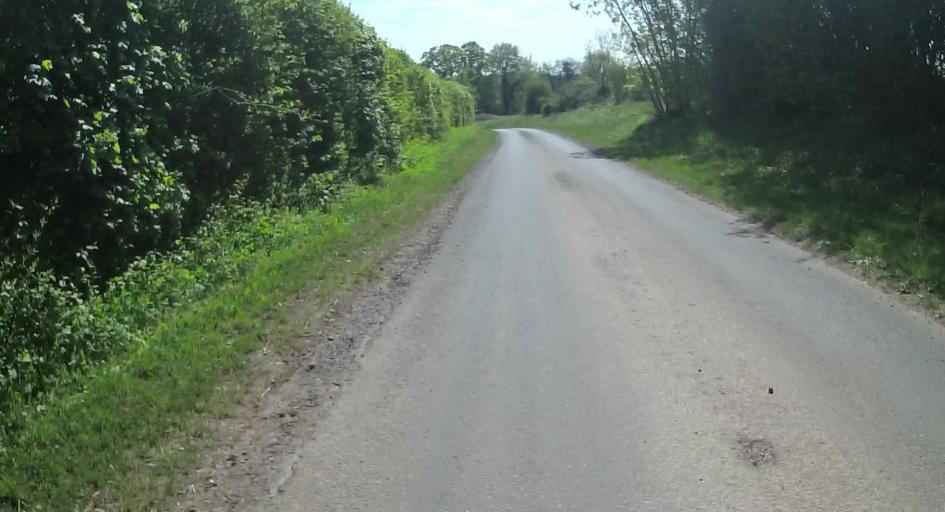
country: GB
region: England
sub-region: Hampshire
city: Four Marks
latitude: 51.1266
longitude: -1.0946
